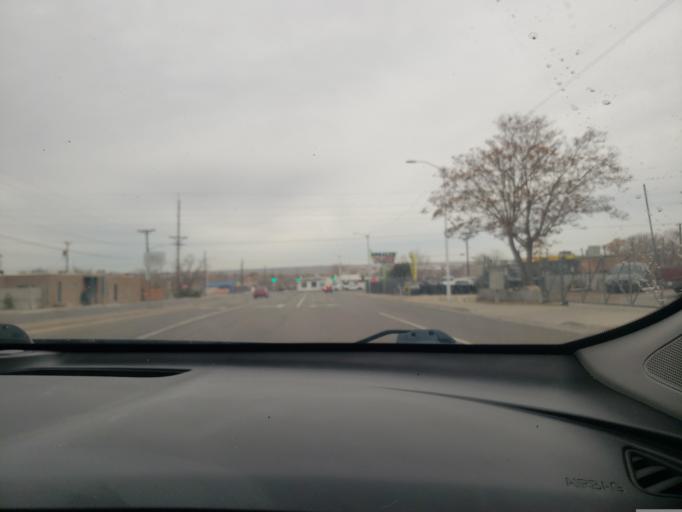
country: US
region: New Mexico
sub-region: Bernalillo County
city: Albuquerque
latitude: 35.0611
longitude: -106.6435
